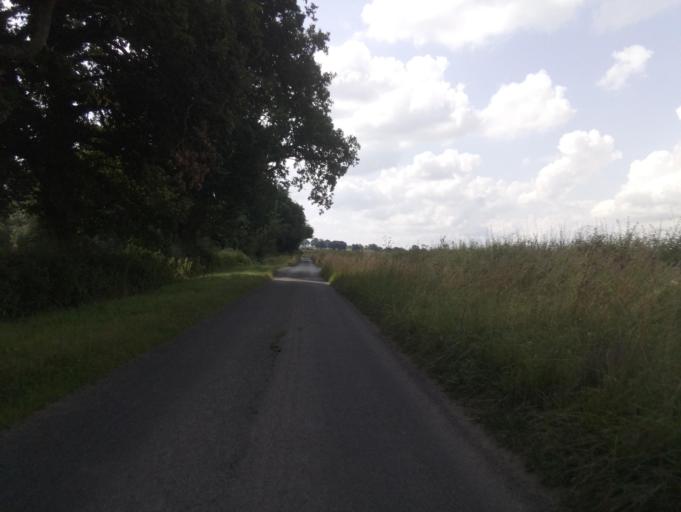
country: GB
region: England
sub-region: Wiltshire
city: Malmesbury
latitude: 51.5692
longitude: -2.1233
